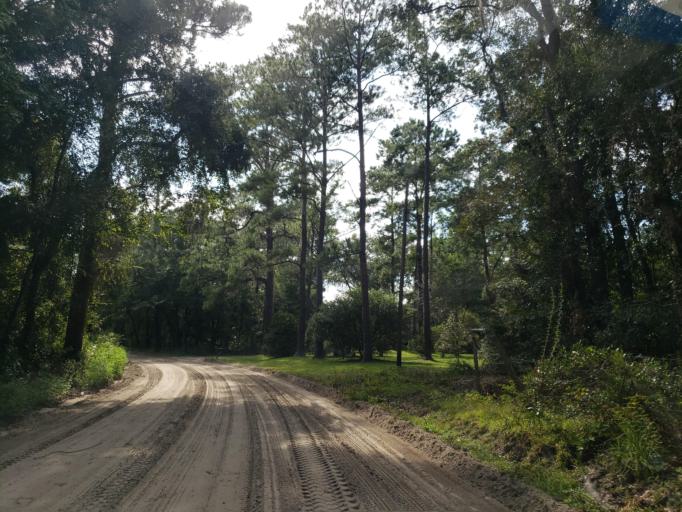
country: US
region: Georgia
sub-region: Echols County
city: Statenville
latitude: 30.6221
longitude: -83.2108
